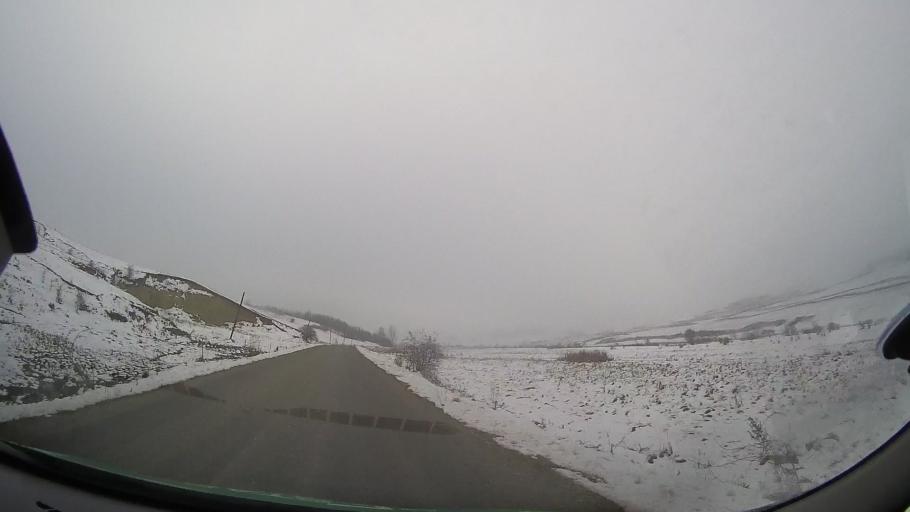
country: RO
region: Bacau
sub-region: Comuna Vultureni
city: Vultureni
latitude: 46.3155
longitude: 27.2930
